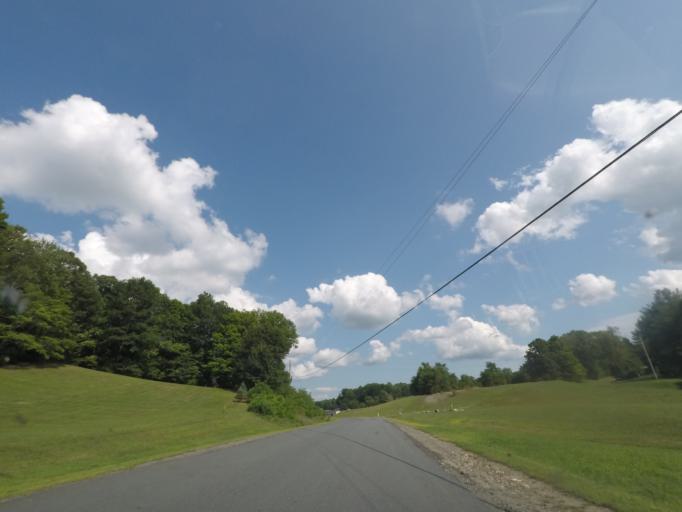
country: US
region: New York
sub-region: Rensselaer County
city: West Sand Lake
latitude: 42.6388
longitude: -73.5855
